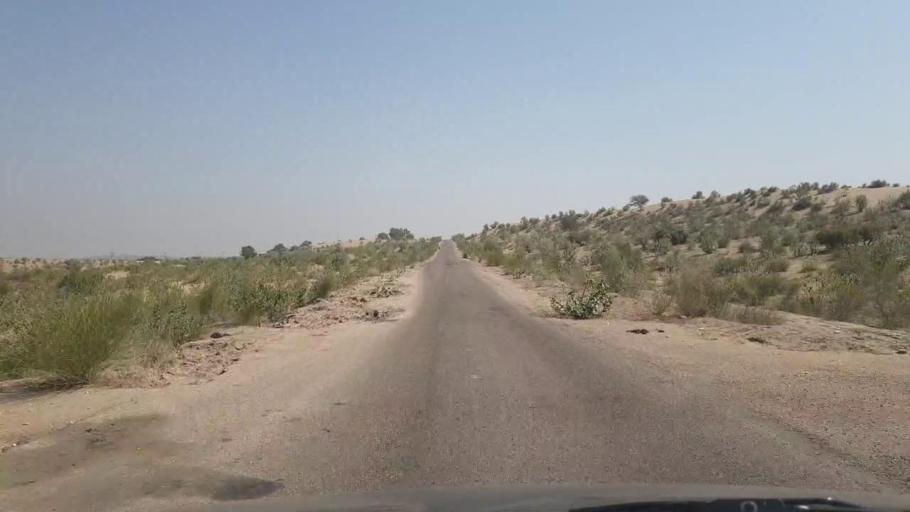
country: PK
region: Sindh
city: Chor
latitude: 25.6410
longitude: 70.0866
